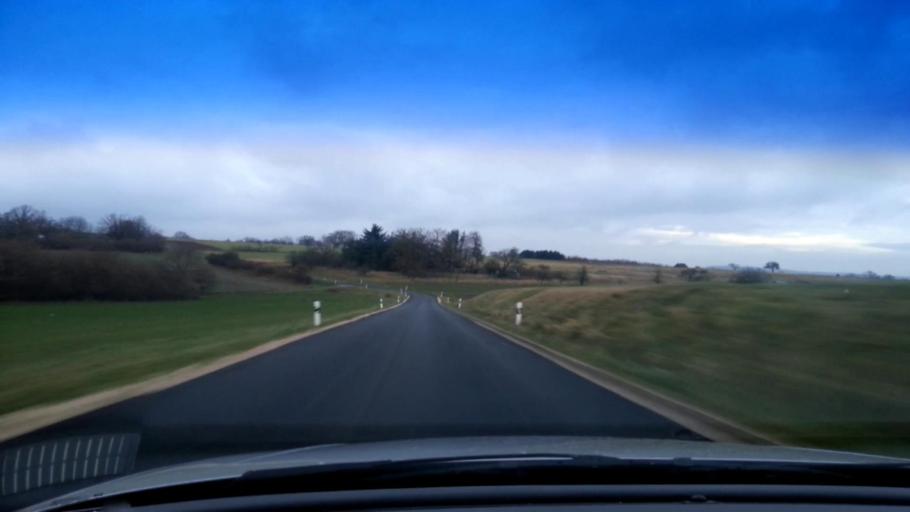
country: DE
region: Bavaria
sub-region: Upper Franconia
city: Viereth-Trunstadt
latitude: 49.9086
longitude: 10.7763
